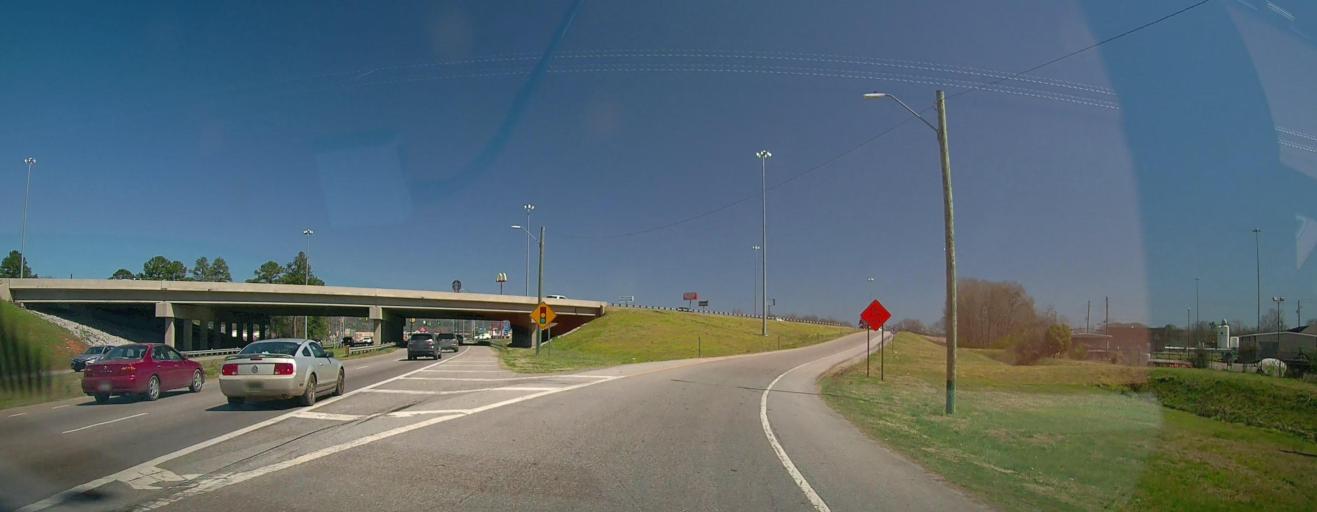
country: US
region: Alabama
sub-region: Calhoun County
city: Oxford
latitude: 33.6040
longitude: -85.8313
